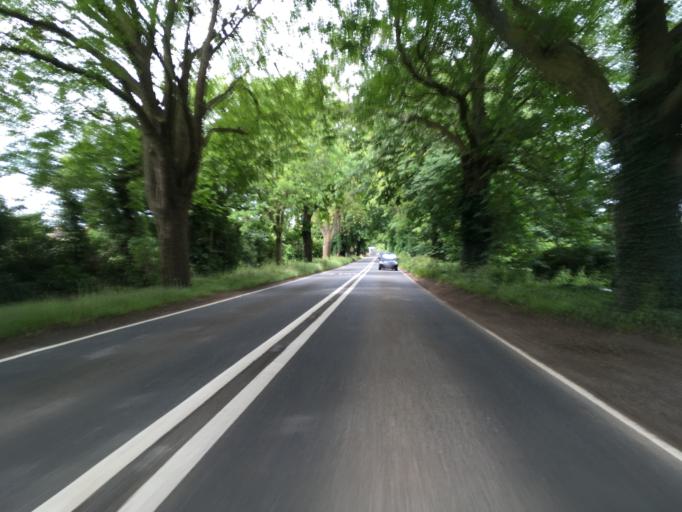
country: GB
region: England
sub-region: Oxfordshire
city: Chipping Norton
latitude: 51.9445
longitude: -1.5303
